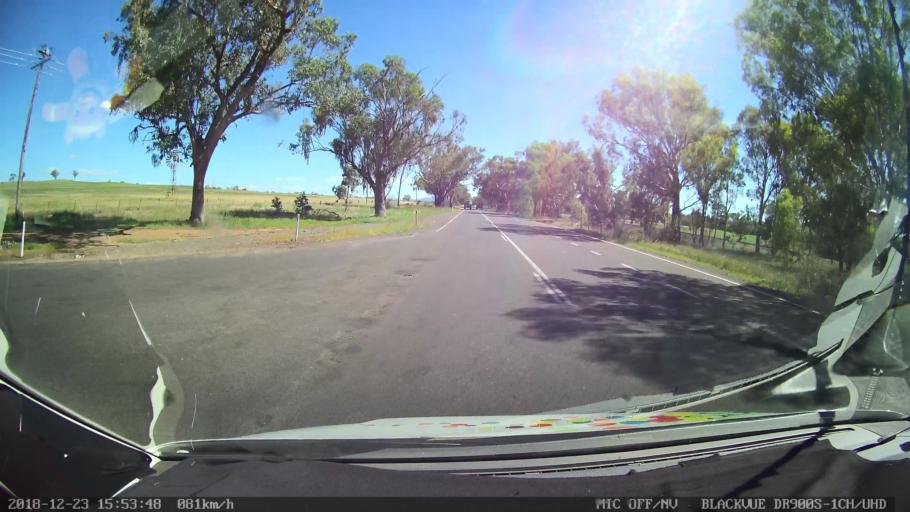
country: AU
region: New South Wales
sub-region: Tamworth Municipality
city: Phillip
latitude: -31.1378
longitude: 150.8791
